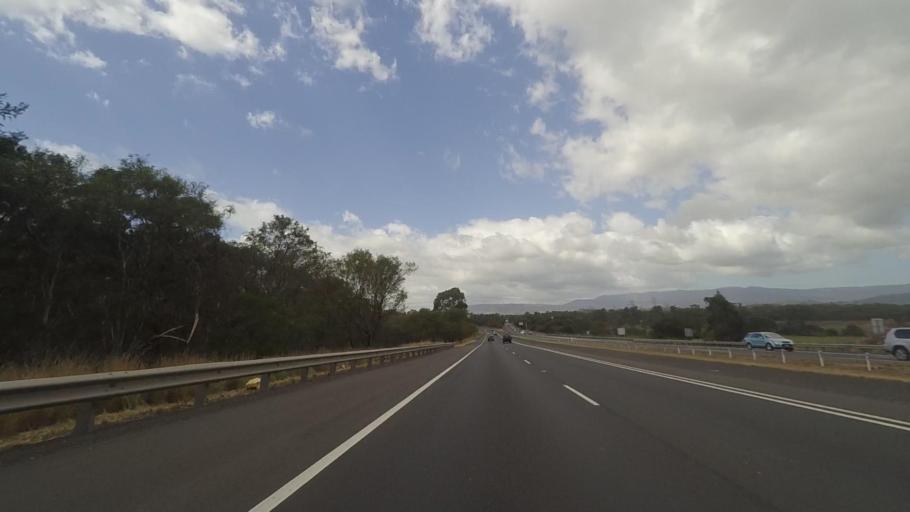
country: AU
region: New South Wales
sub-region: Wollongong
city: Dapto
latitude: -34.5241
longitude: 150.7881
